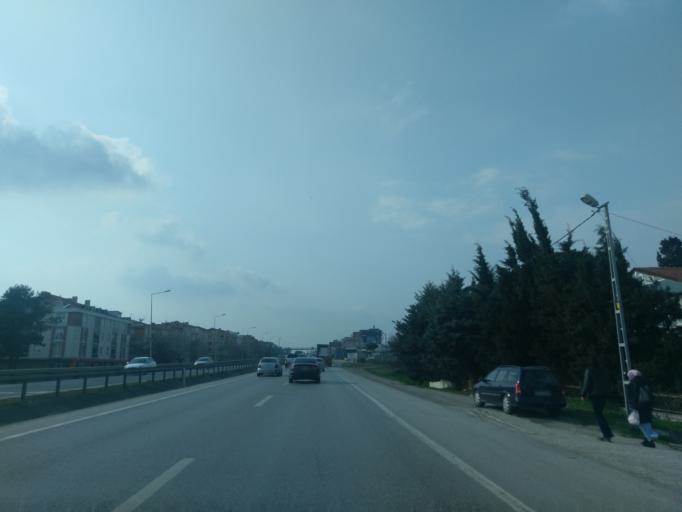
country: TR
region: Istanbul
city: Selimpasa
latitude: 41.0550
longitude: 28.3742
